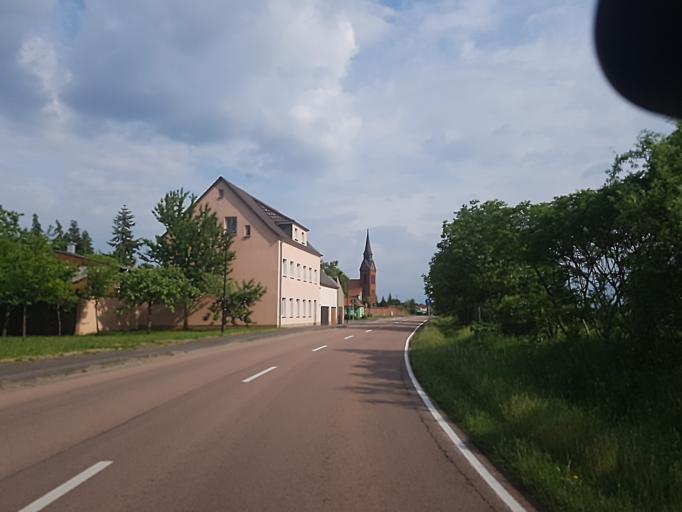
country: DE
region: Saxony-Anhalt
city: Klieken
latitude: 51.9140
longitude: 12.4095
